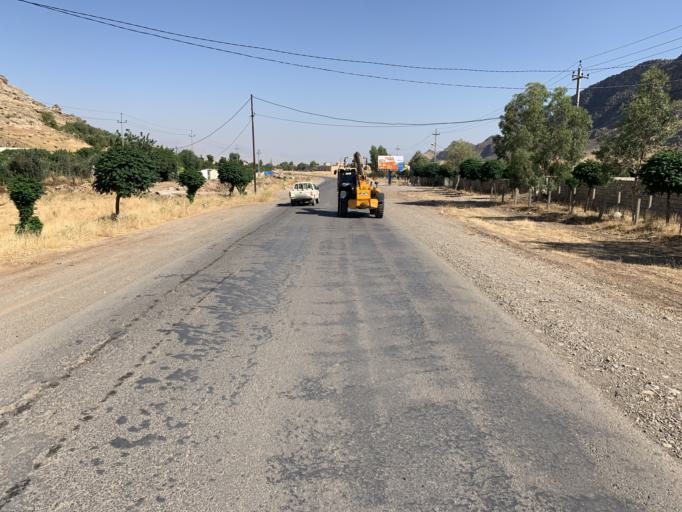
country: IQ
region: As Sulaymaniyah
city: Raniye
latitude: 36.2685
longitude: 44.8382
